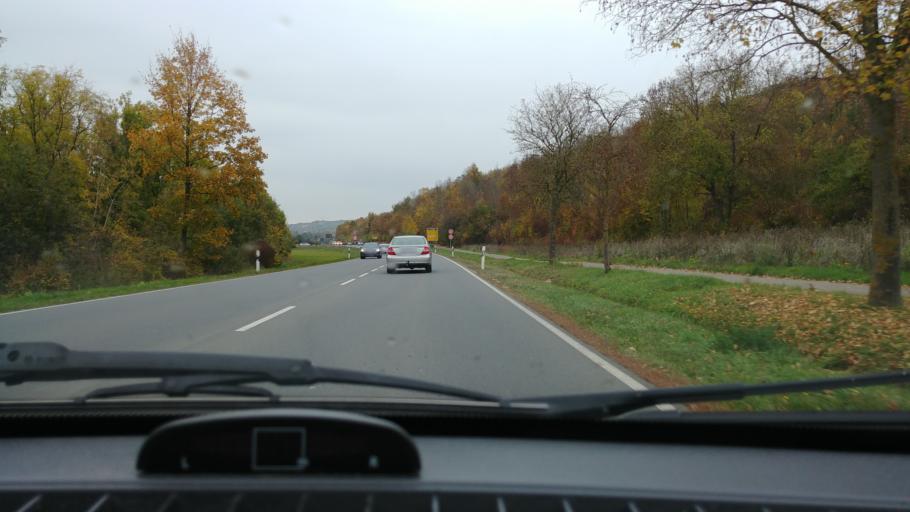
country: DE
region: Baden-Wuerttemberg
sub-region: Regierungsbezirk Stuttgart
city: Lauda-Konigshofen
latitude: 49.5681
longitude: 9.7141
